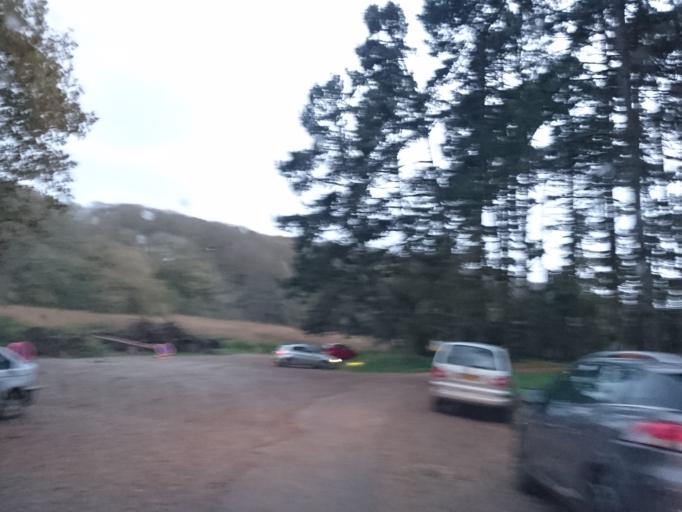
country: FR
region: Brittany
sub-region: Departement du Finistere
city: Le Conquet
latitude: 48.3671
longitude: -4.7470
